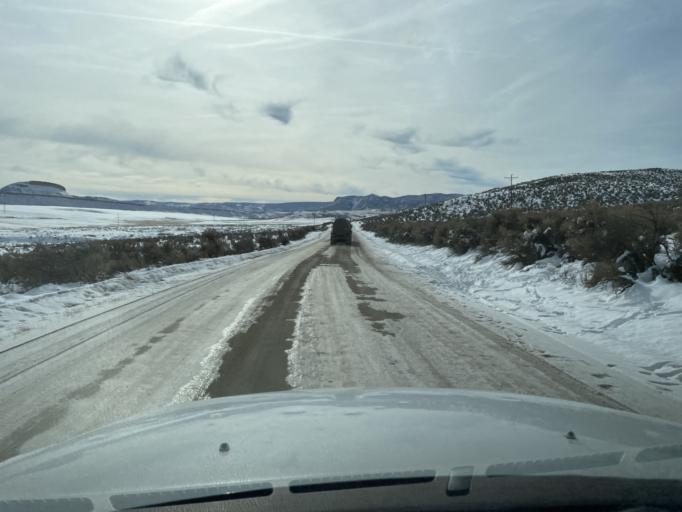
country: US
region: Colorado
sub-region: Moffat County
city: Craig
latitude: 40.3305
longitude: -107.6871
